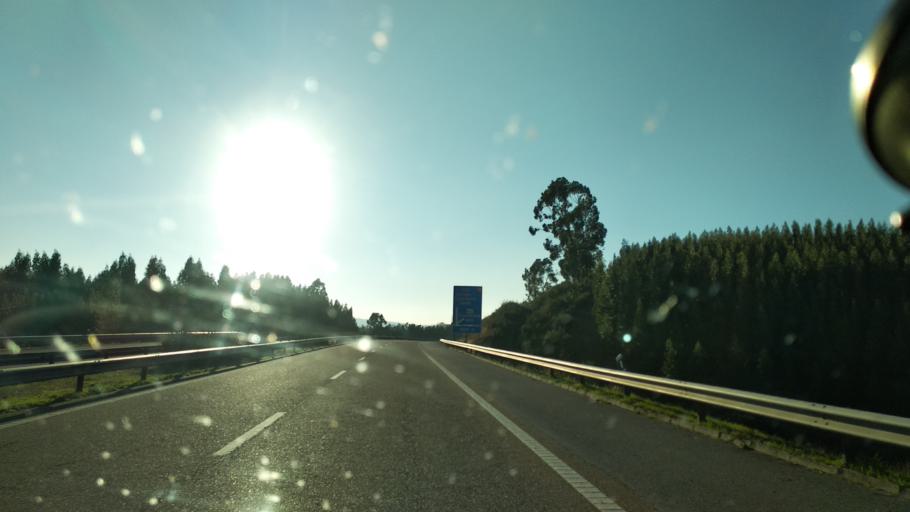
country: PT
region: Santarem
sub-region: Constancia
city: Constancia
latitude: 39.4896
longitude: -8.3116
